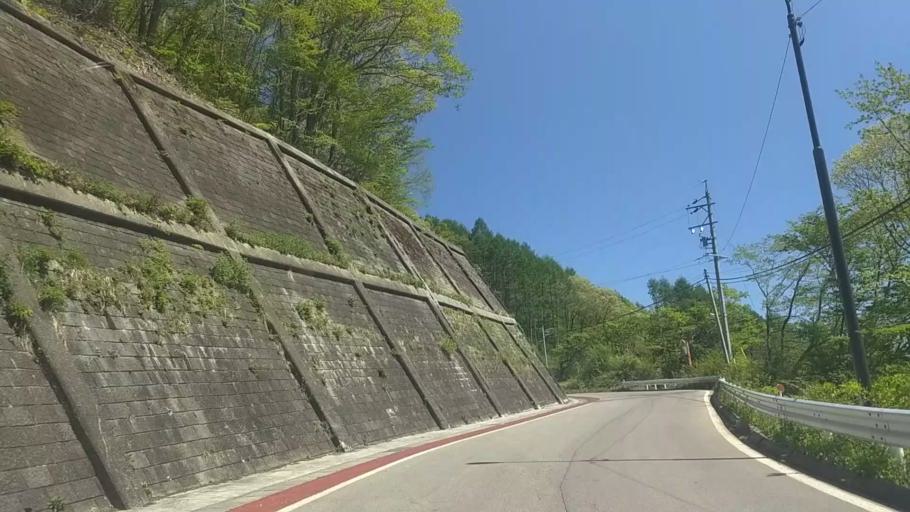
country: JP
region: Yamanashi
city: Nirasaki
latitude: 35.9213
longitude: 138.4450
